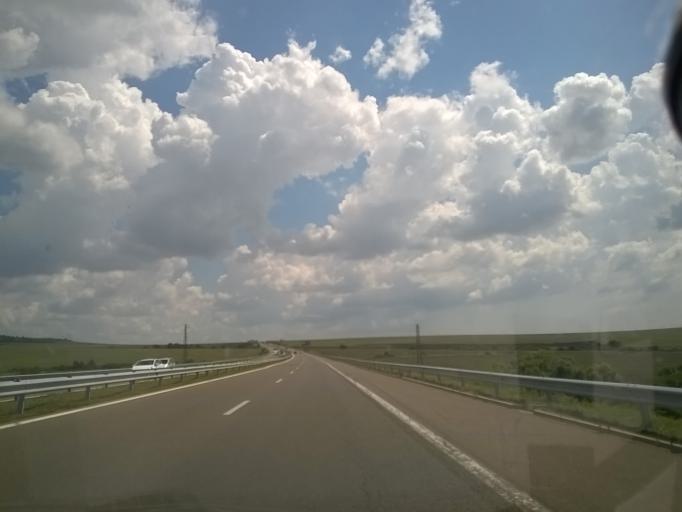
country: BG
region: Burgas
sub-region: Obshtina Karnobat
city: Karnobat
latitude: 42.5870
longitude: 27.0936
